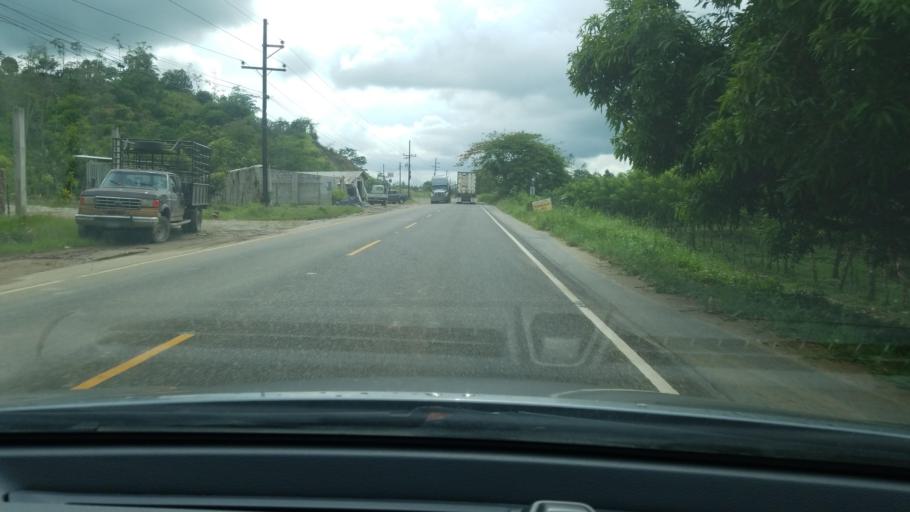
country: HN
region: Cortes
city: Potrerillos
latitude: 15.5947
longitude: -88.3130
